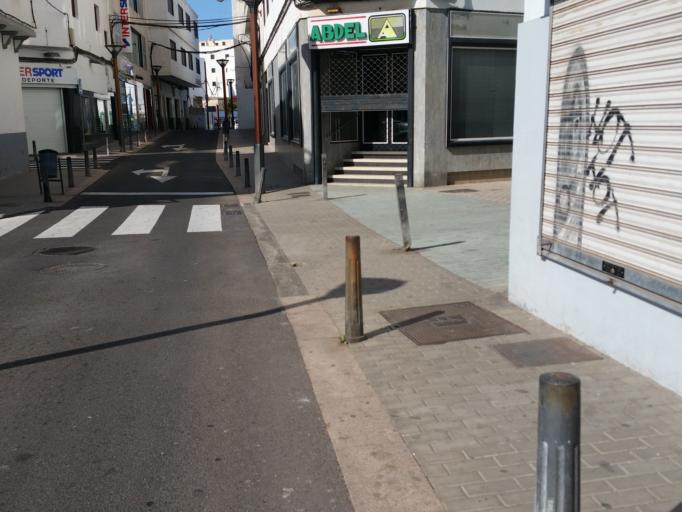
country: ES
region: Canary Islands
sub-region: Provincia de Las Palmas
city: Arrecife
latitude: 28.9613
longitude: -13.5501
